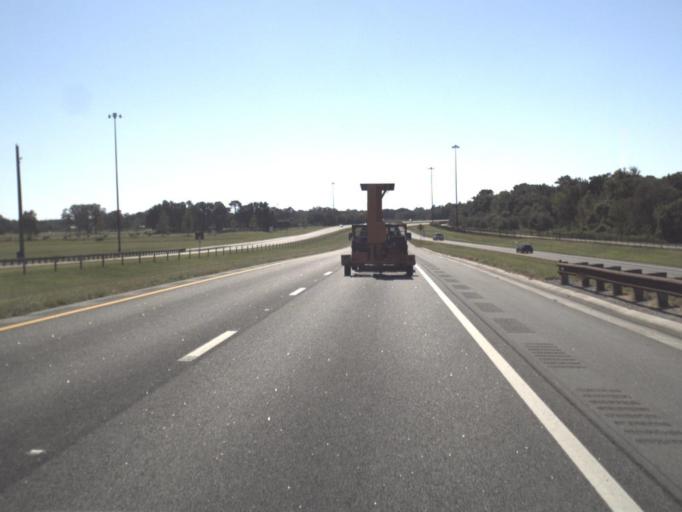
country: US
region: Florida
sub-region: Hernando County
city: Masaryktown
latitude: 28.4318
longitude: -82.4853
